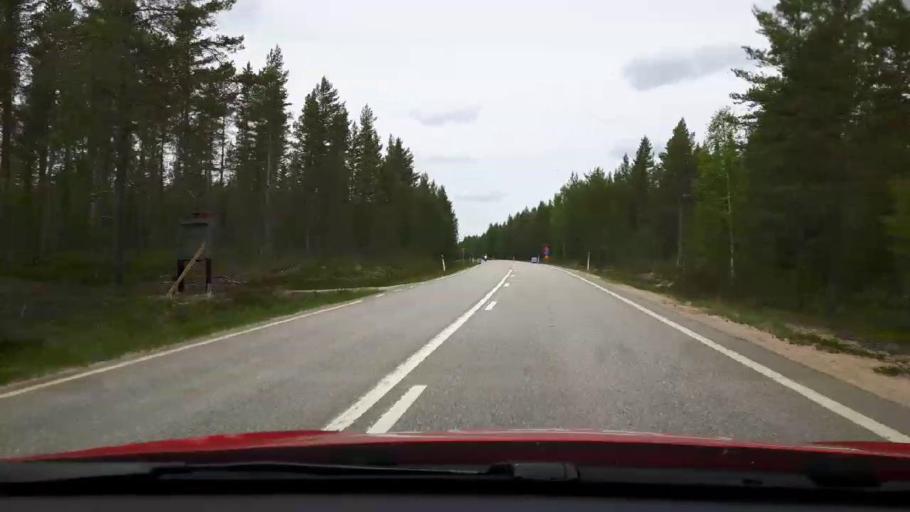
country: SE
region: Jaemtland
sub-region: Harjedalens Kommun
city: Sveg
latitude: 62.0745
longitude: 14.2690
